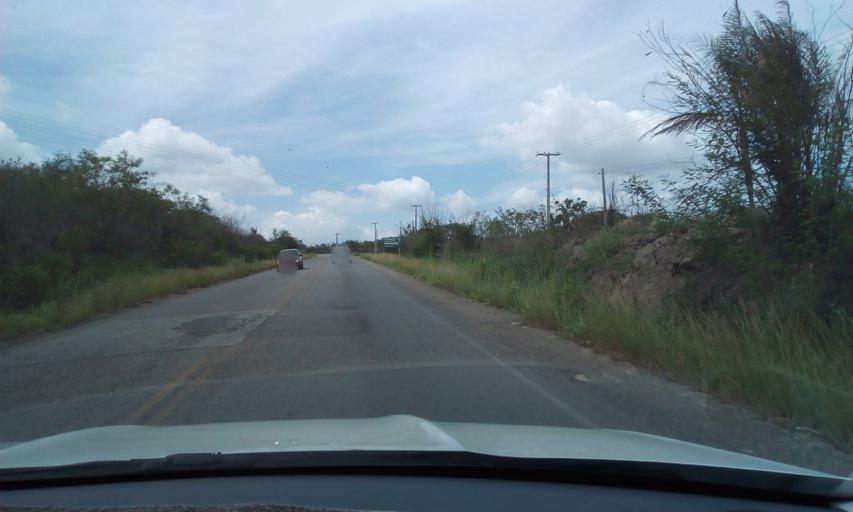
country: BR
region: Pernambuco
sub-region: Bezerros
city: Bezerros
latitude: -8.2784
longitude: -35.7425
